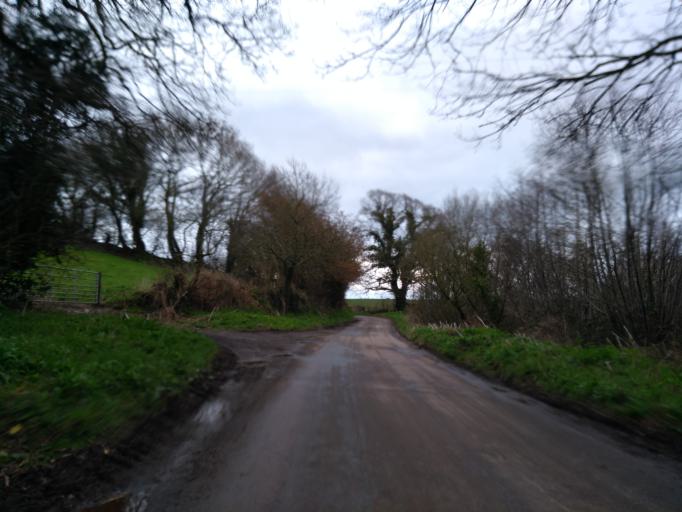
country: GB
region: England
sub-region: Devon
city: Crediton
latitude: 50.7849
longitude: -3.6074
